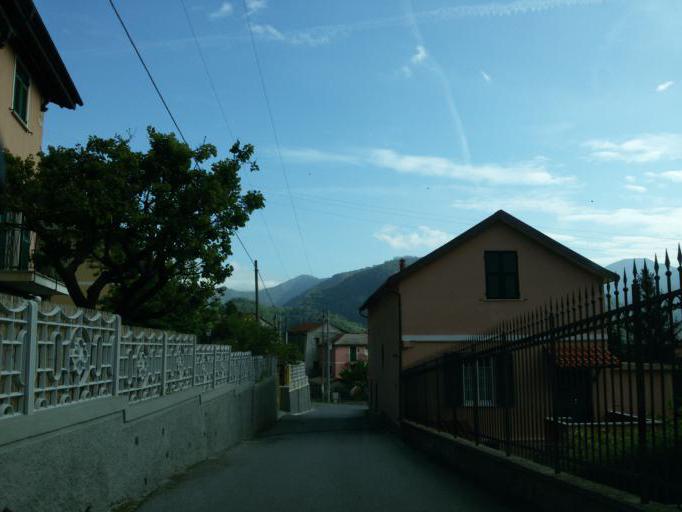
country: IT
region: Liguria
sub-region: Provincia di Genova
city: Piccarello
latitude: 44.4456
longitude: 8.9891
